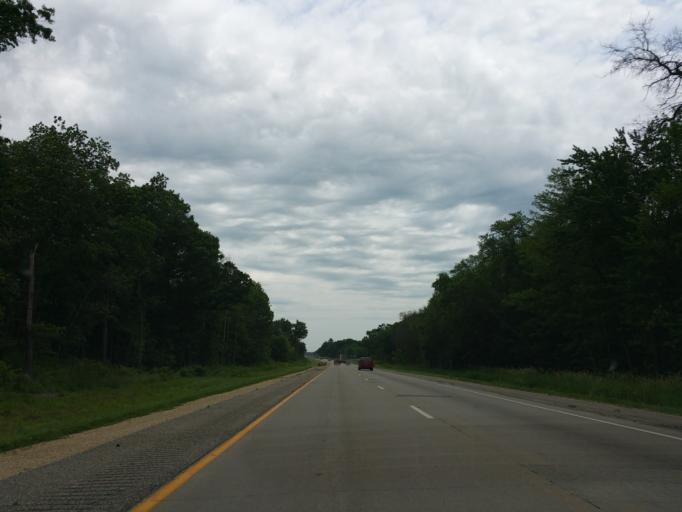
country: US
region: Wisconsin
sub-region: Juneau County
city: Mauston
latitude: 43.7722
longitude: -90.0069
